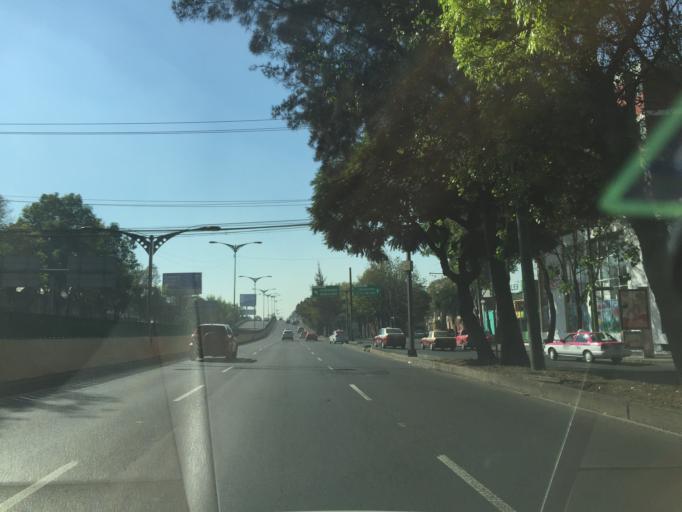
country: MX
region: Mexico City
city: Azcapotzalco
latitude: 19.4817
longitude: -99.1885
